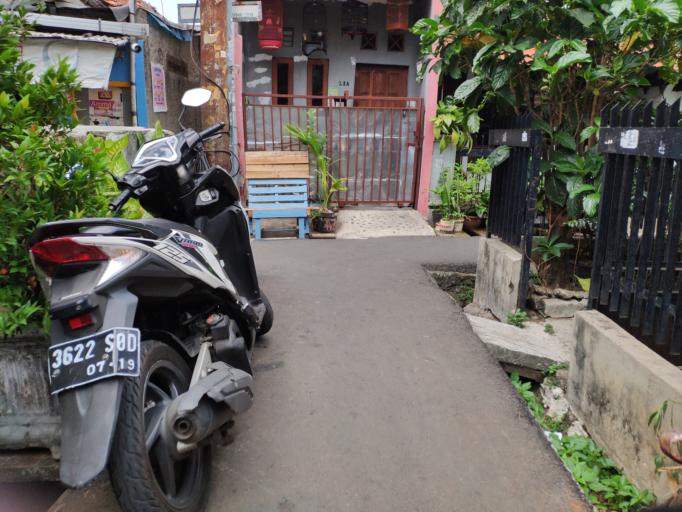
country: ID
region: Jakarta Raya
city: Jakarta
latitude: -6.1968
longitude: 106.8602
